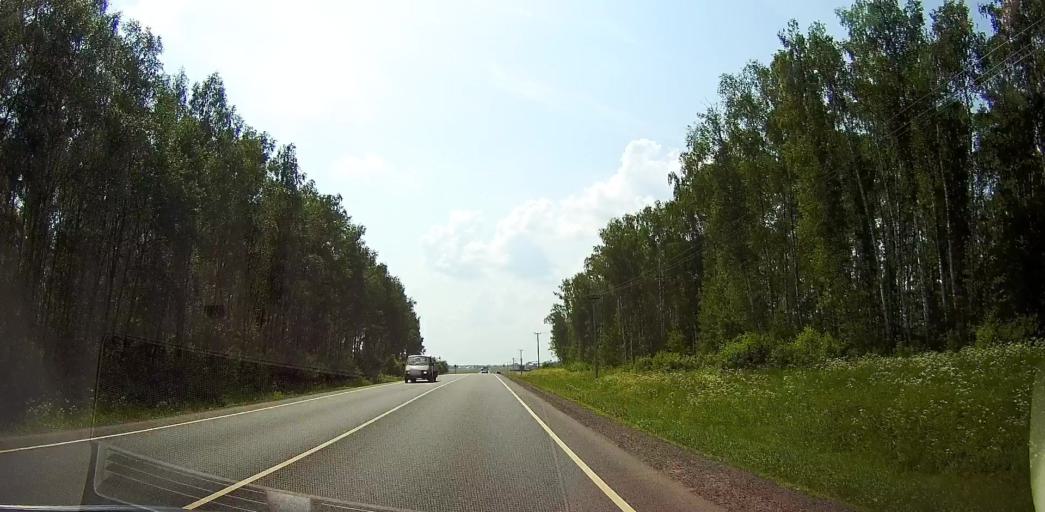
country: RU
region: Moskovskaya
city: Meshcherino
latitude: 55.1593
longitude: 38.3123
